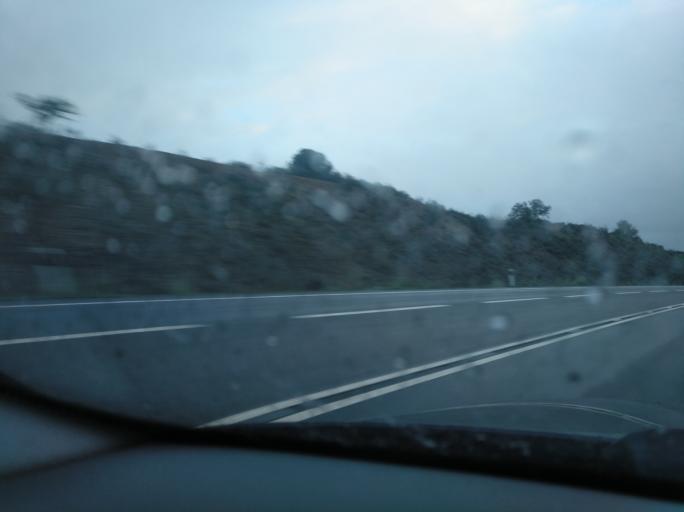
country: PT
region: Faro
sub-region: Castro Marim
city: Castro Marim
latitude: 37.2871
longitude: -7.4861
